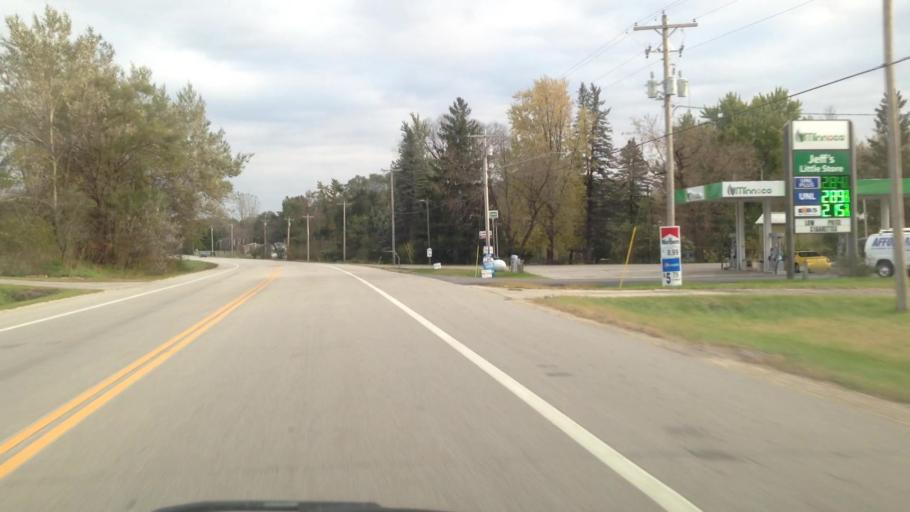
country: US
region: Minnesota
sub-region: Olmsted County
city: Rochester
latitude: 43.9744
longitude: -92.3931
